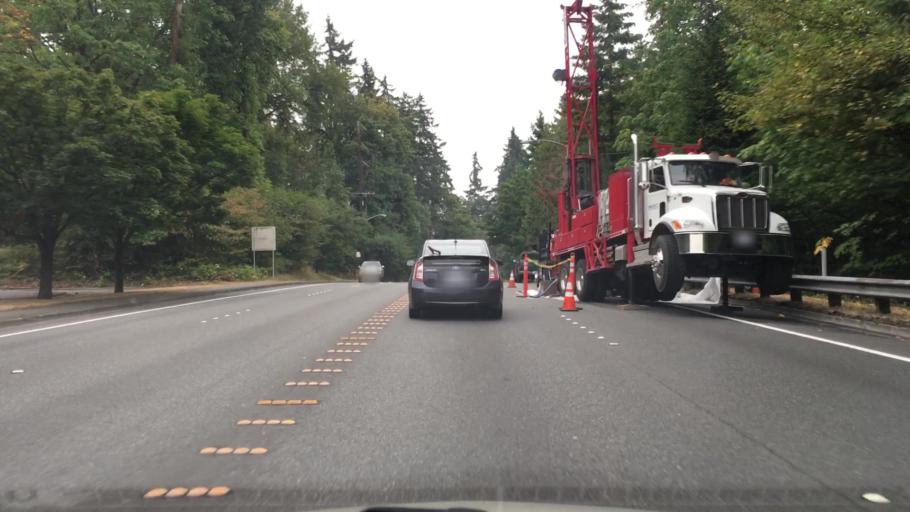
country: US
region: Washington
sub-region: King County
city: Newport
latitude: 47.5632
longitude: -122.1702
